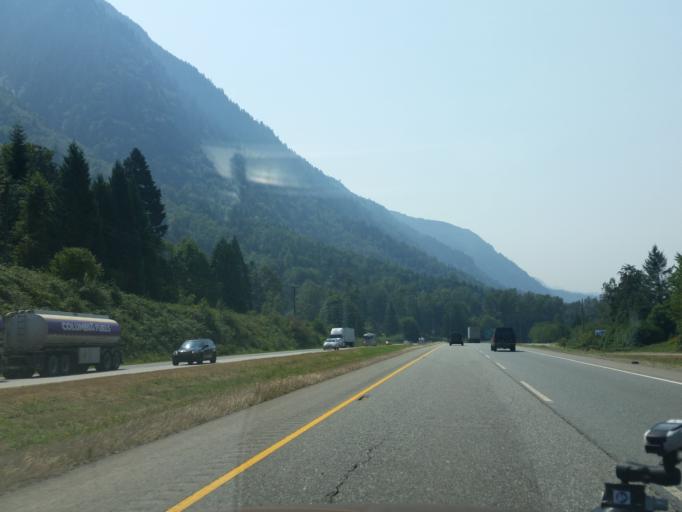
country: CA
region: British Columbia
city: Agassiz
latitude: 49.2110
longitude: -121.7067
